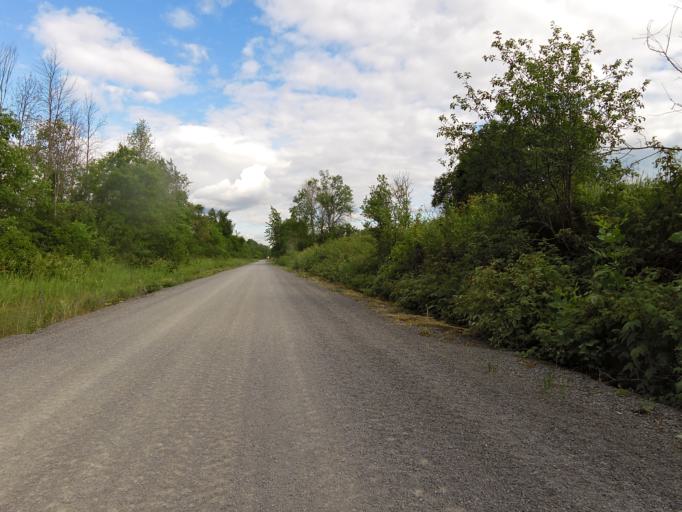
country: CA
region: Ontario
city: Arnprior
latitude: 45.3052
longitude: -76.2715
